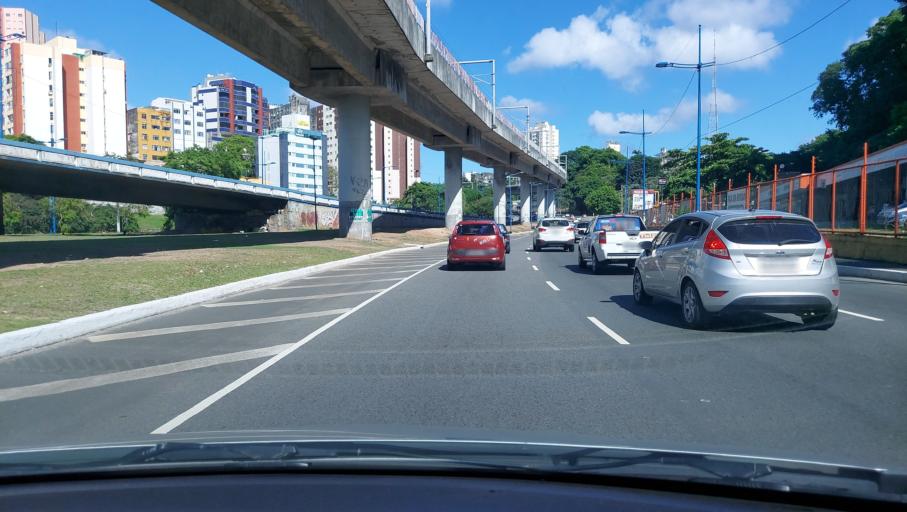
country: BR
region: Bahia
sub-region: Salvador
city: Salvador
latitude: -12.9824
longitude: -38.4945
